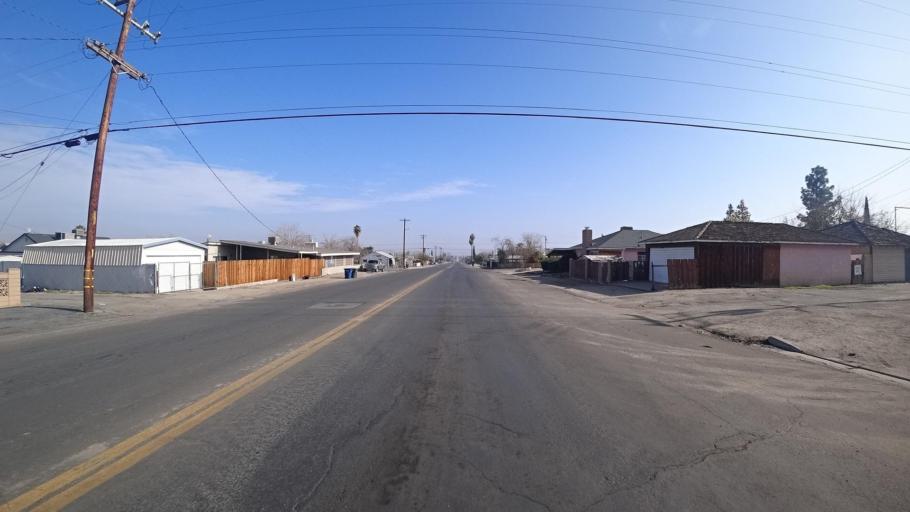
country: US
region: California
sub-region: Kern County
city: Ford City
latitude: 35.1545
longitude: -119.4559
